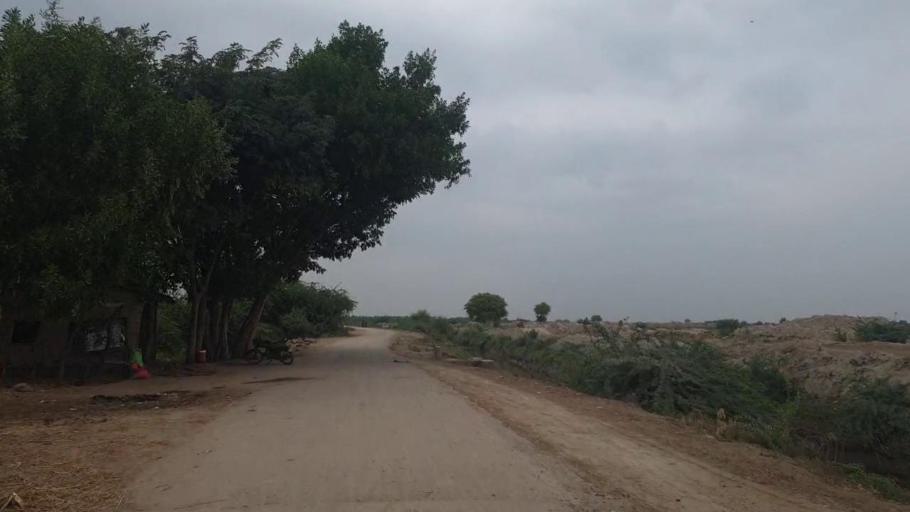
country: PK
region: Sindh
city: Badin
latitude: 24.6327
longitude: 68.6818
